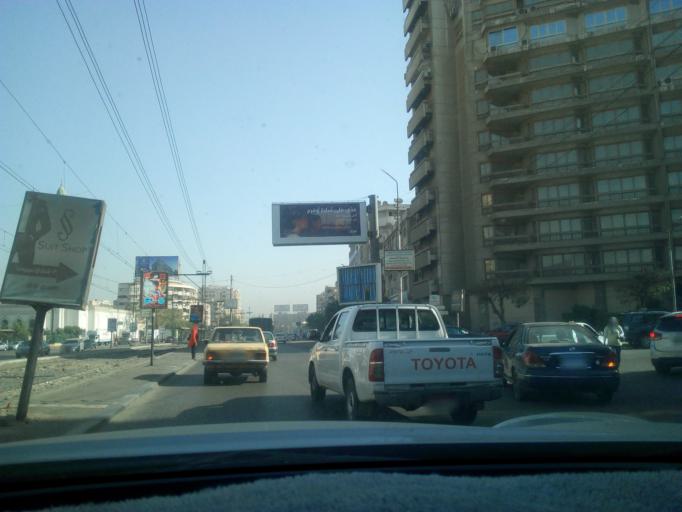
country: EG
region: Muhafazat al Qahirah
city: Cairo
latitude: 30.0995
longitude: 31.3235
